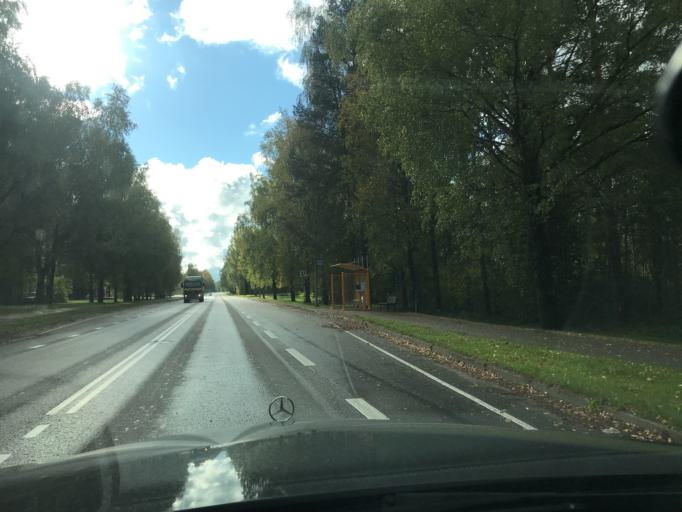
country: EE
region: Valgamaa
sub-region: Torva linn
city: Torva
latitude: 57.9934
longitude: 25.9378
